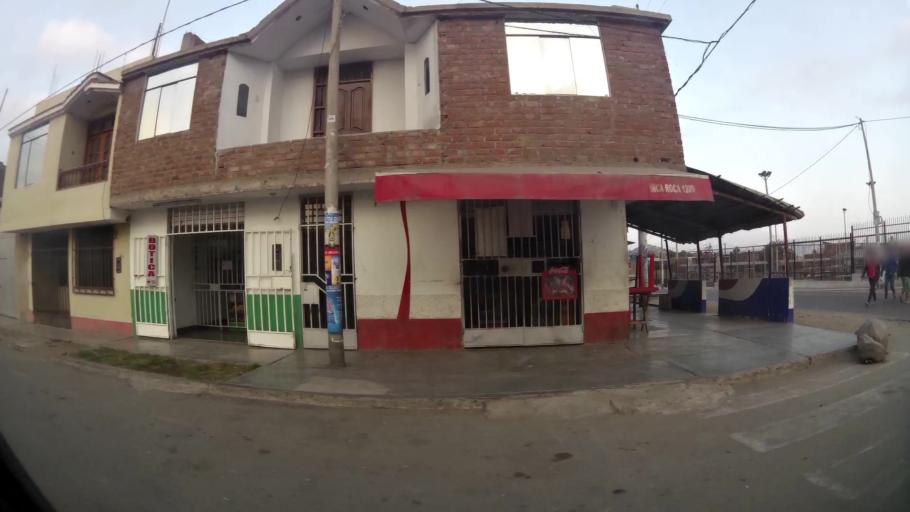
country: PE
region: La Libertad
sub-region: Provincia de Trujillo
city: El Porvenir
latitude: -8.0711
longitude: -79.0061
